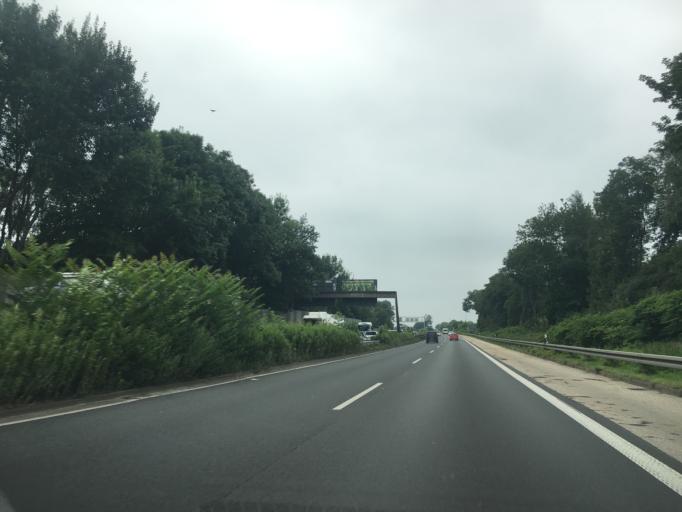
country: DE
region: North Rhine-Westphalia
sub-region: Regierungsbezirk Arnsberg
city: Herne
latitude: 51.5439
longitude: 7.1874
